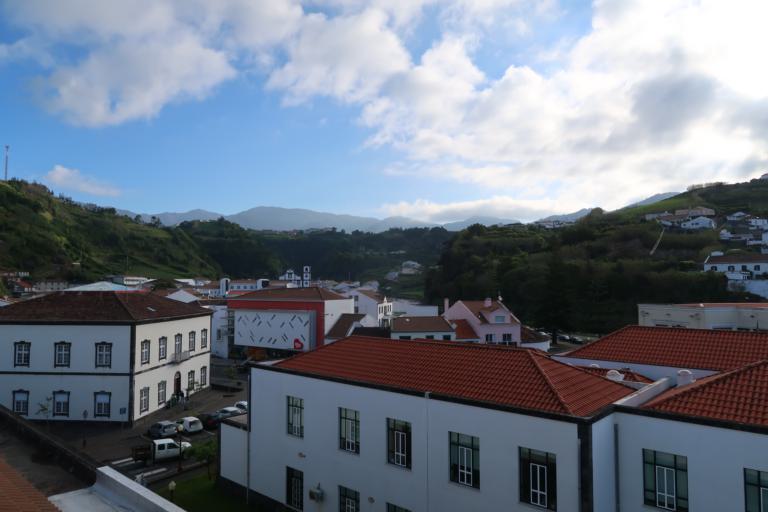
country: PT
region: Azores
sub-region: Povoacao
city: Furnas
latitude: 37.7460
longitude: -25.2461
